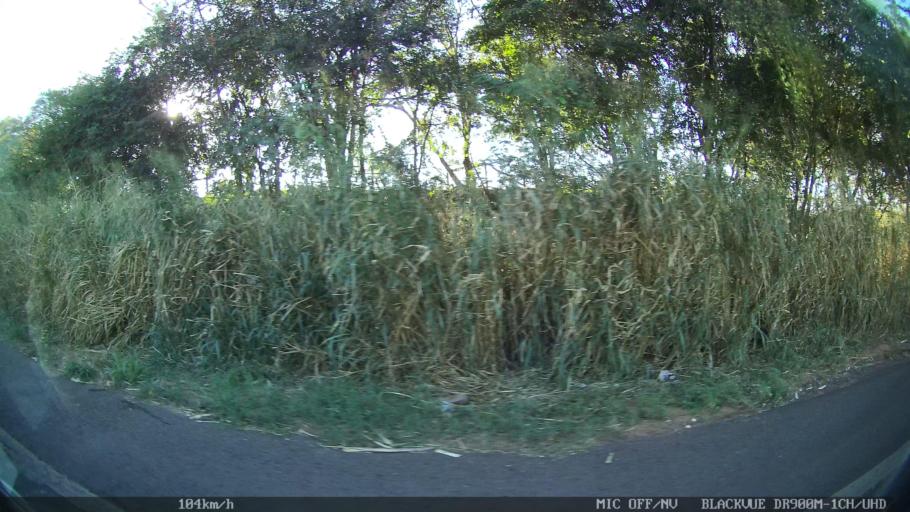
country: BR
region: Sao Paulo
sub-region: Guapiacu
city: Guapiacu
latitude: -20.7701
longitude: -49.2139
